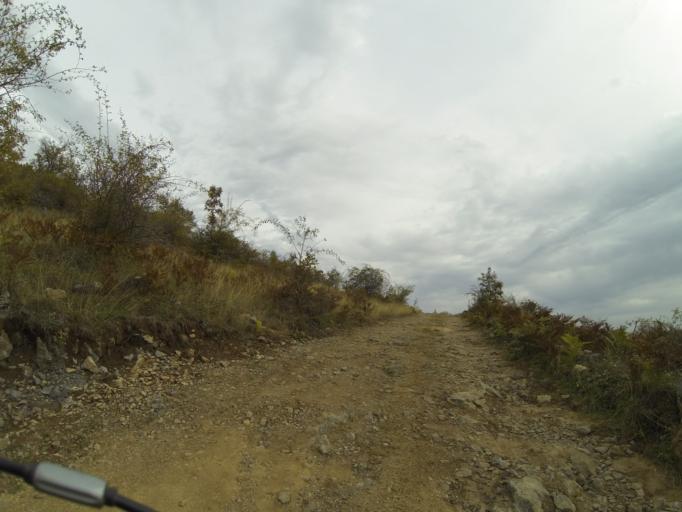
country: RO
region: Gorj
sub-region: Comuna Tismana
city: Sohodol
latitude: 45.0684
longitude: 22.8616
